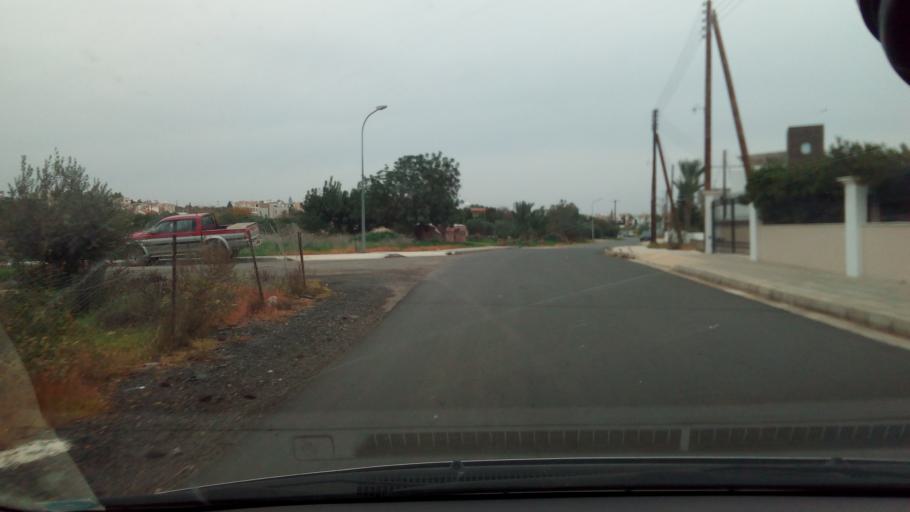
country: CY
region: Pafos
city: Empa
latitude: 34.8019
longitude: 32.4210
